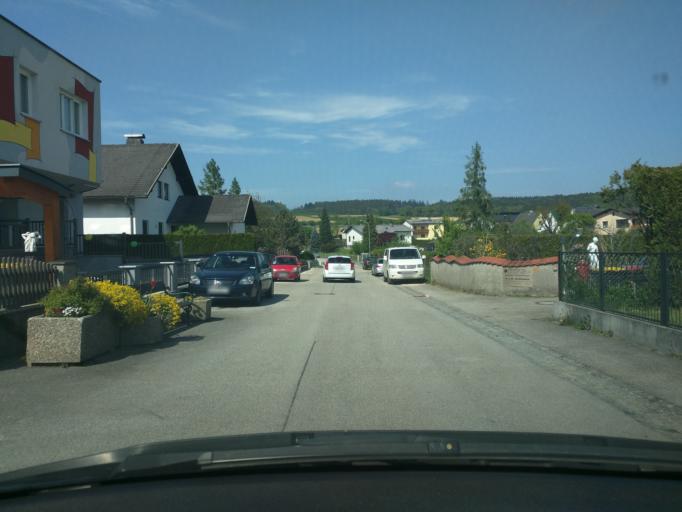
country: AT
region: Lower Austria
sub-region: Politischer Bezirk Melk
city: Blindenmarkt
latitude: 48.1308
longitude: 14.9852
